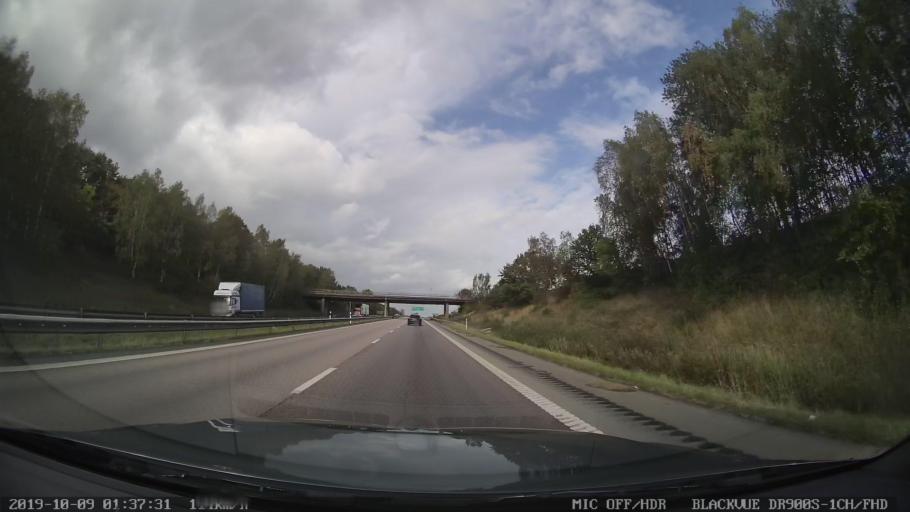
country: SE
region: Skane
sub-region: Helsingborg
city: Gantofta
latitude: 56.0016
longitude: 12.7800
